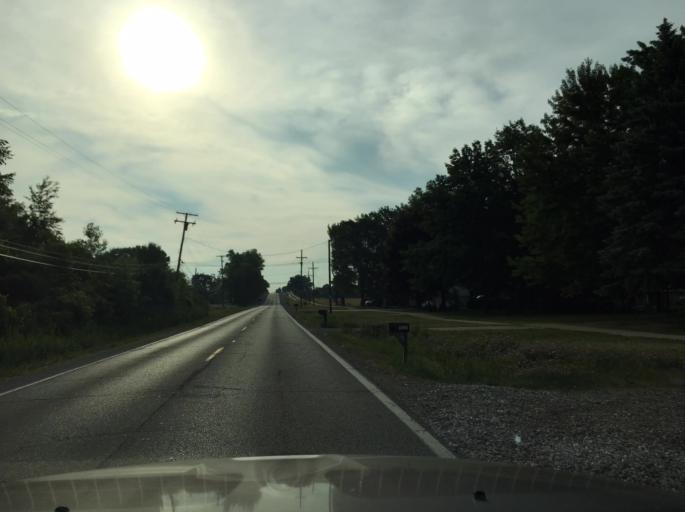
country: US
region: Michigan
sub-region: Macomb County
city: Utica
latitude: 42.6408
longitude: -83.0198
